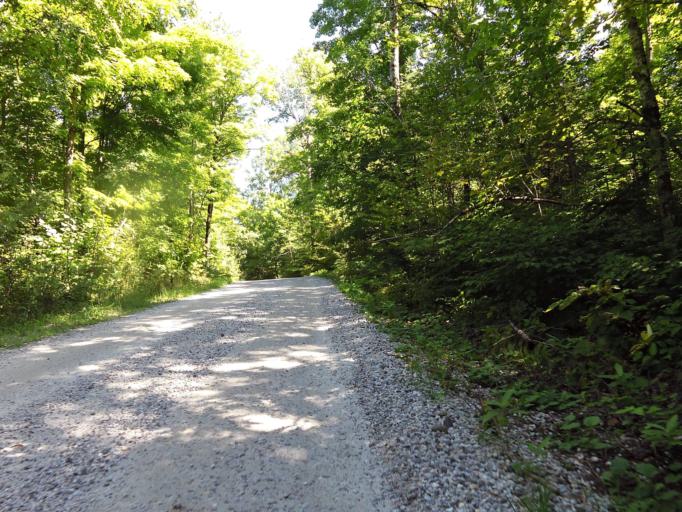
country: CA
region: Ontario
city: Renfrew
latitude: 45.1286
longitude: -76.6909
